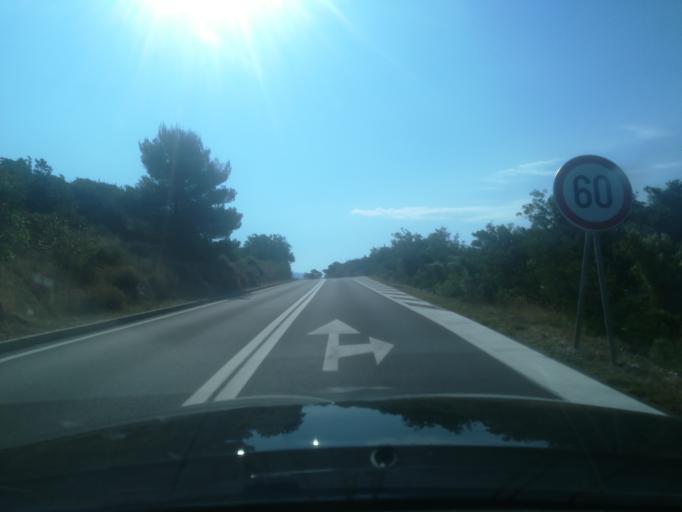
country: HR
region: Primorsko-Goranska
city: Banjol
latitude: 44.7068
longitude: 14.8378
